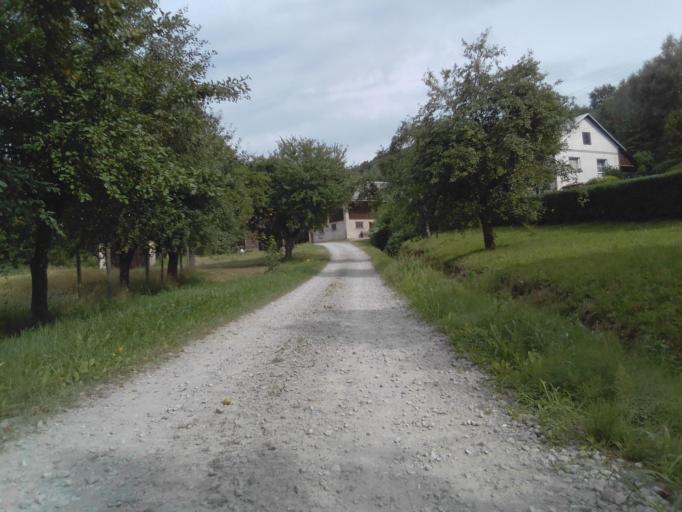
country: PL
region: Subcarpathian Voivodeship
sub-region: Powiat strzyzowski
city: Frysztak
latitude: 49.8755
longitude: 21.5652
